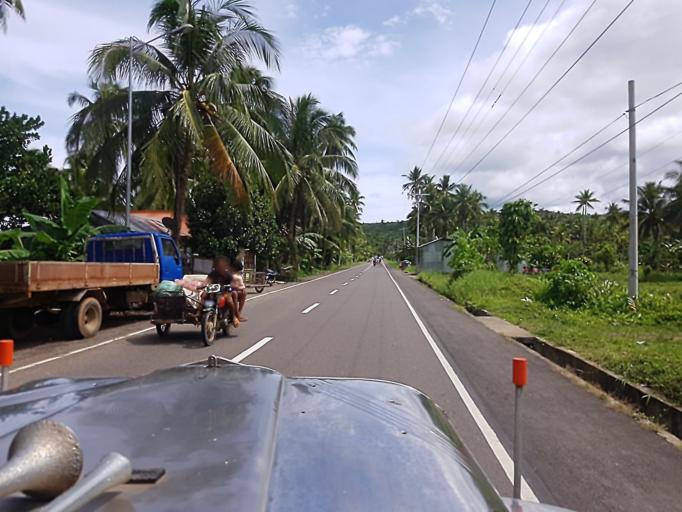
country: PH
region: Eastern Visayas
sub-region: Province of Eastern Samar
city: General MacArthur
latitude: 11.2375
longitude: 125.5350
